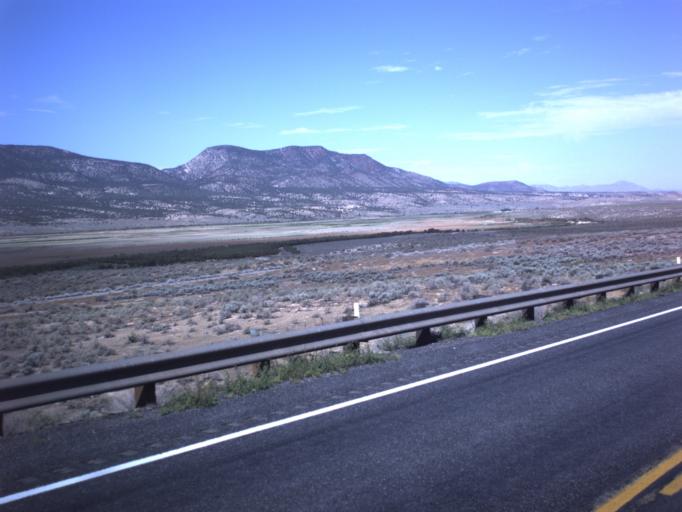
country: US
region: Utah
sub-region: Sanpete County
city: Gunnison
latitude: 39.2838
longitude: -111.8816
